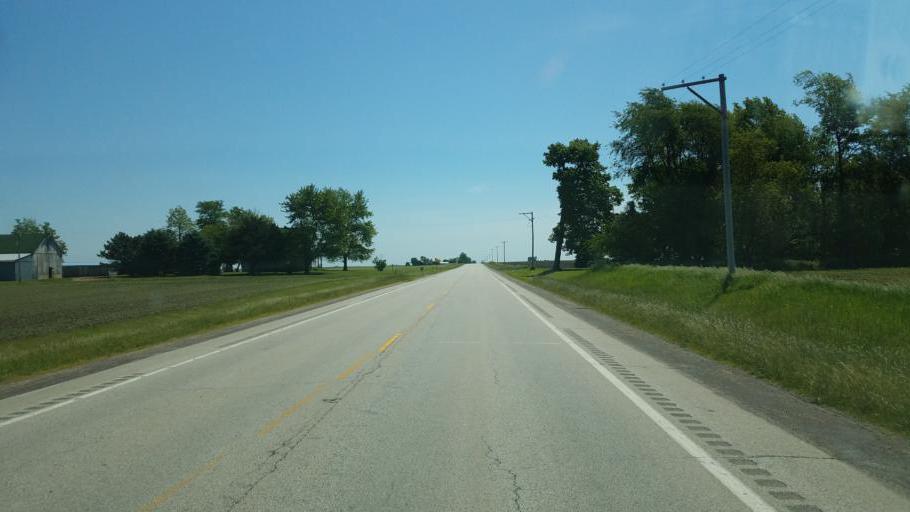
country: US
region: Illinois
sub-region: McLean County
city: Heyworth
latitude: 40.3123
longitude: -88.9156
